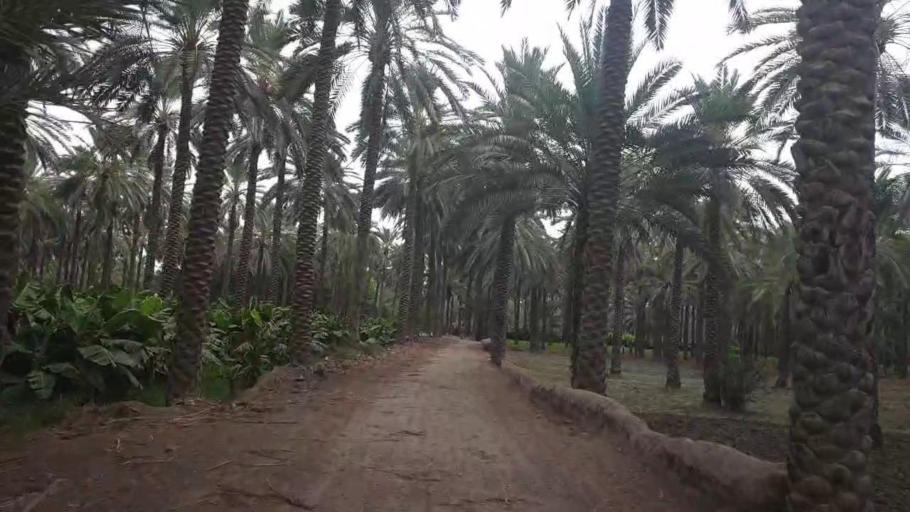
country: PK
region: Sindh
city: Khairpur
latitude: 27.5803
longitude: 68.7488
